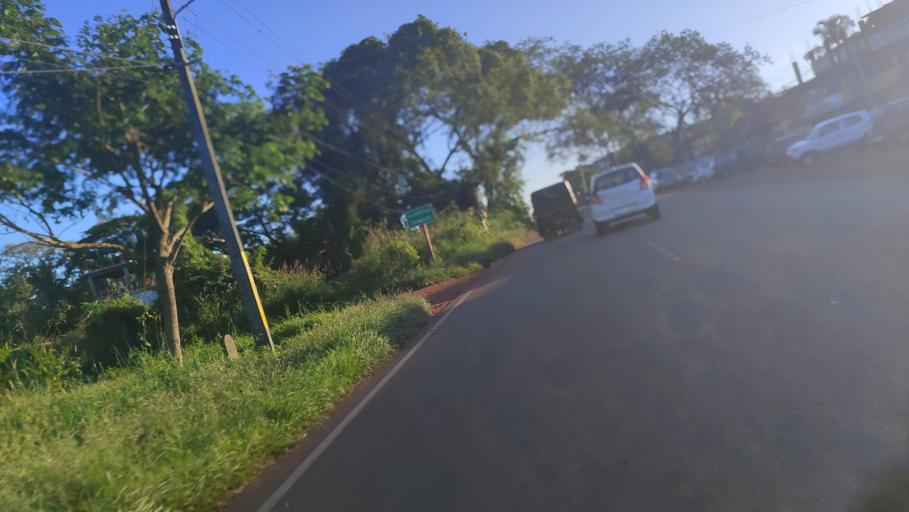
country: IN
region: Kerala
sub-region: Kasaragod District
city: Kasaragod
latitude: 12.4660
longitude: 75.0584
